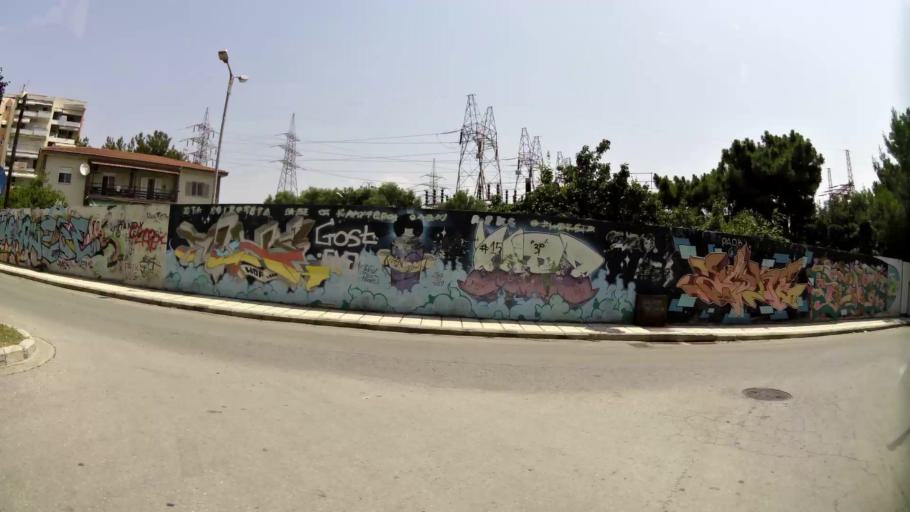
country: GR
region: Central Macedonia
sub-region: Nomos Thessalonikis
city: Evosmos
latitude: 40.6728
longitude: 22.8995
